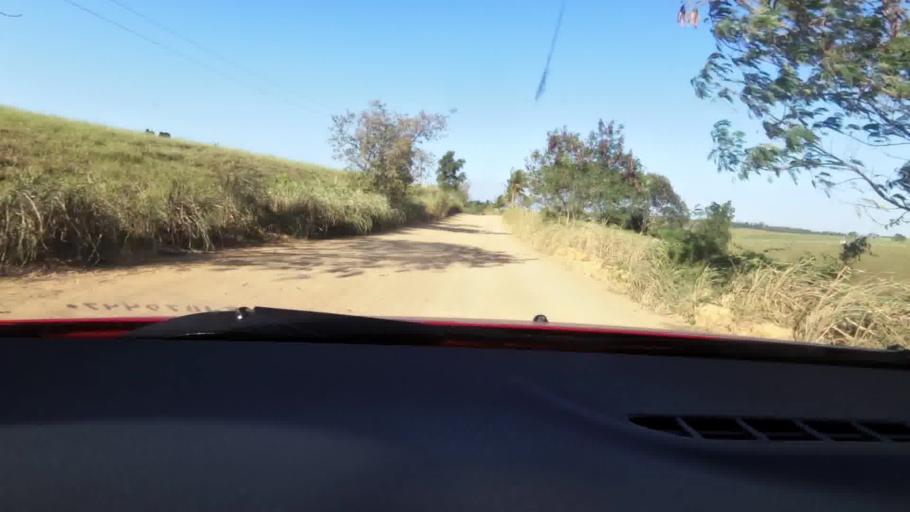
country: BR
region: Espirito Santo
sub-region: Guarapari
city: Guarapari
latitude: -20.5371
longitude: -40.4462
